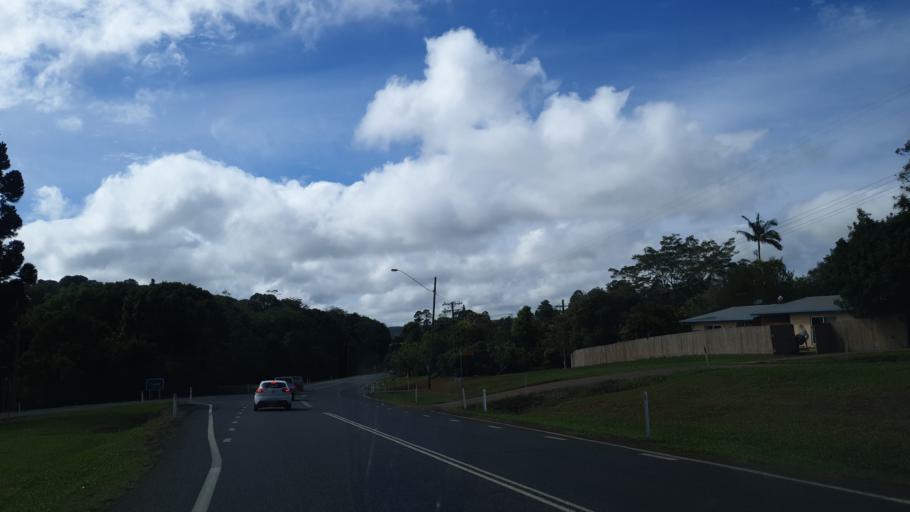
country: AU
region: Queensland
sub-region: Tablelands
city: Atherton
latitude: -17.3511
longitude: 145.5821
